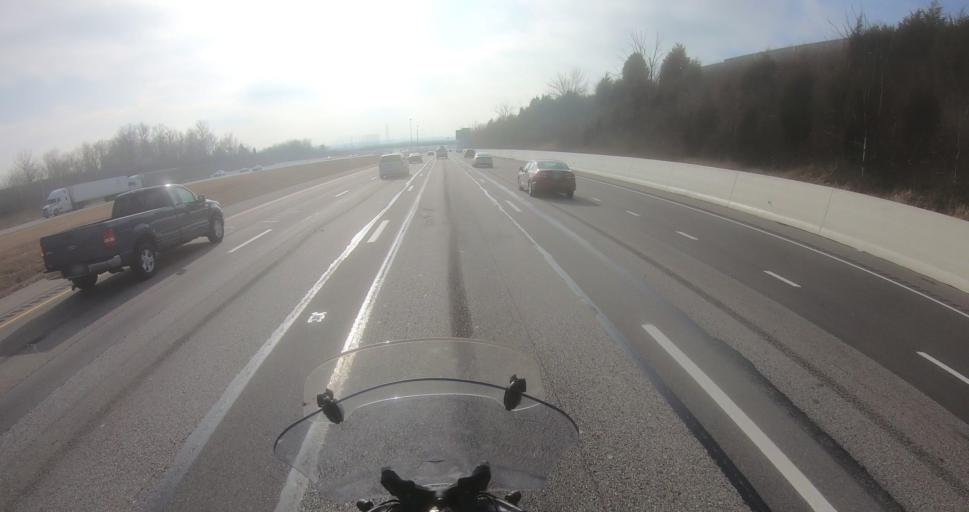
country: US
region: Ohio
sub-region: Butler County
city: Beckett Ridge
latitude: 39.3308
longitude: -84.4157
